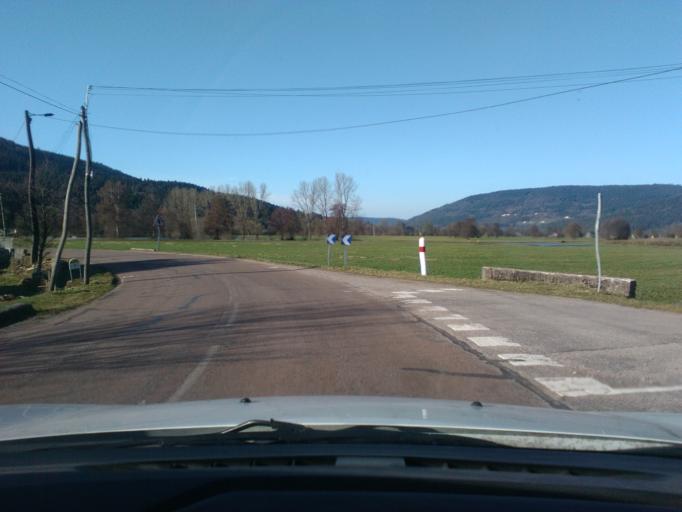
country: FR
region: Lorraine
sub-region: Departement des Vosges
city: Vecoux
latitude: 47.9840
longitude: 6.6273
